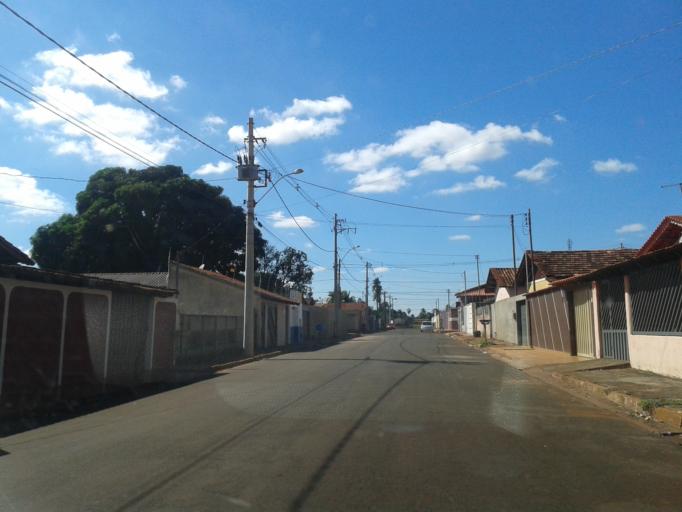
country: BR
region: Minas Gerais
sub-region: Centralina
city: Centralina
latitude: -18.5913
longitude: -49.1986
